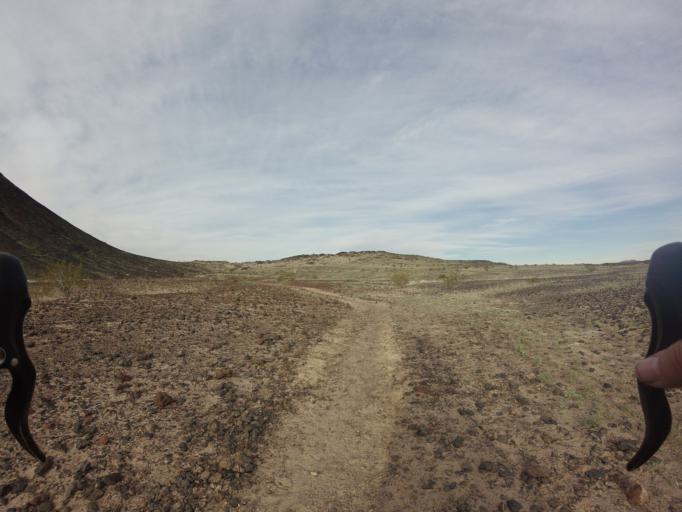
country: US
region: California
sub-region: San Bernardino County
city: Twentynine Palms
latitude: 34.5481
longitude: -115.7893
